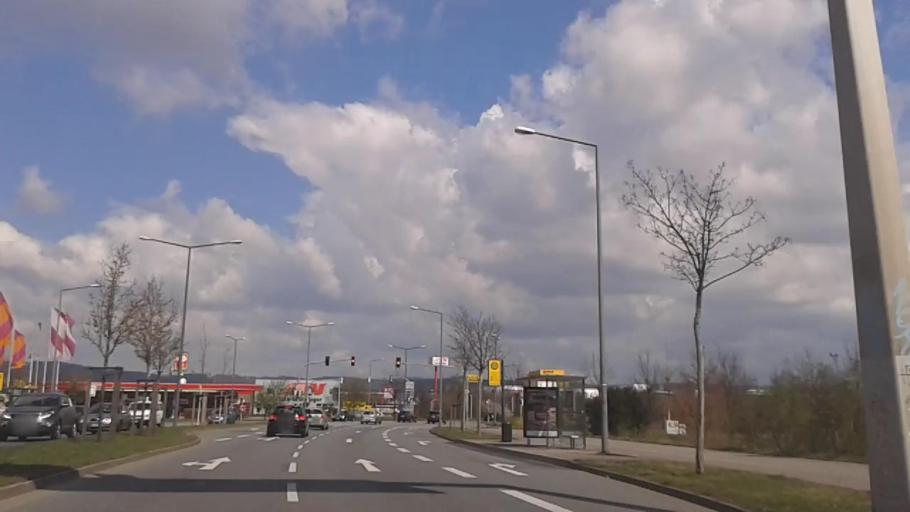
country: DE
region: Saxony
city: Radebeul
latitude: 51.0775
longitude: 13.6905
